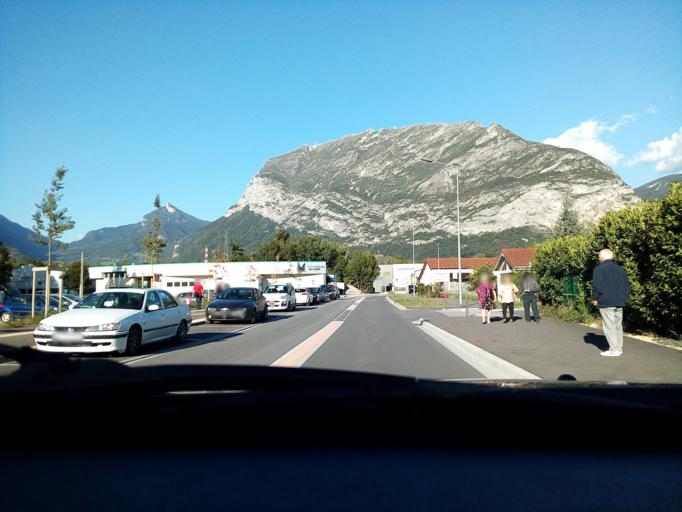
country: FR
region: Rhone-Alpes
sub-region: Departement de l'Isere
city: Sassenage
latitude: 45.2115
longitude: 5.6728
